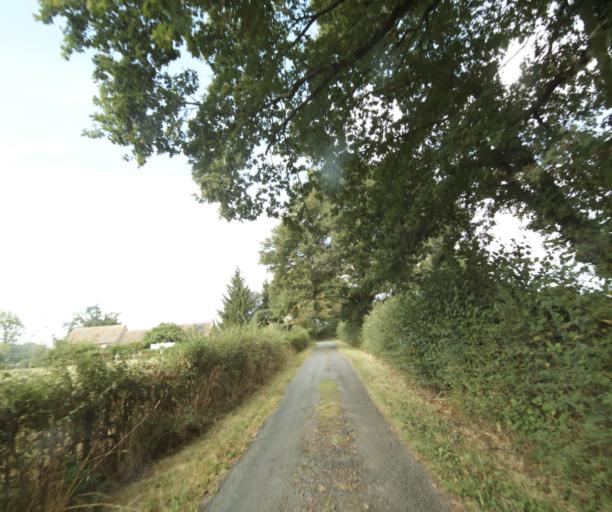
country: FR
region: Bourgogne
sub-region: Departement de Saone-et-Loire
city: Palinges
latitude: 46.4997
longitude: 4.2542
